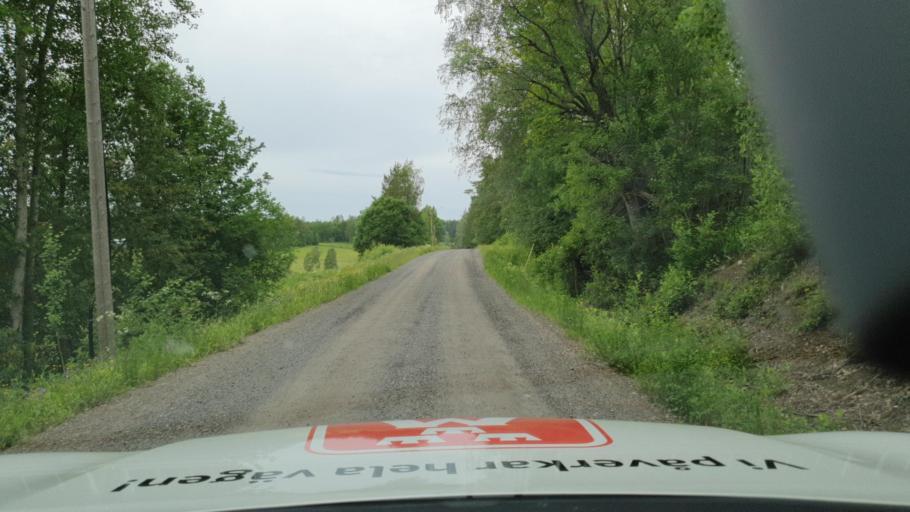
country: SE
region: Vaesterbotten
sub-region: Robertsfors Kommun
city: Robertsfors
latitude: 64.2134
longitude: 20.6886
